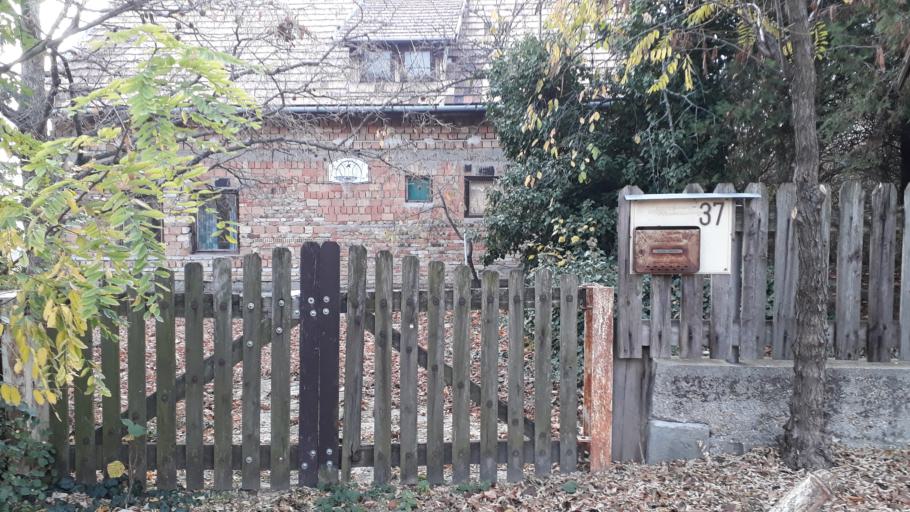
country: HU
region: Pest
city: Budaors
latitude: 47.4722
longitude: 18.9681
